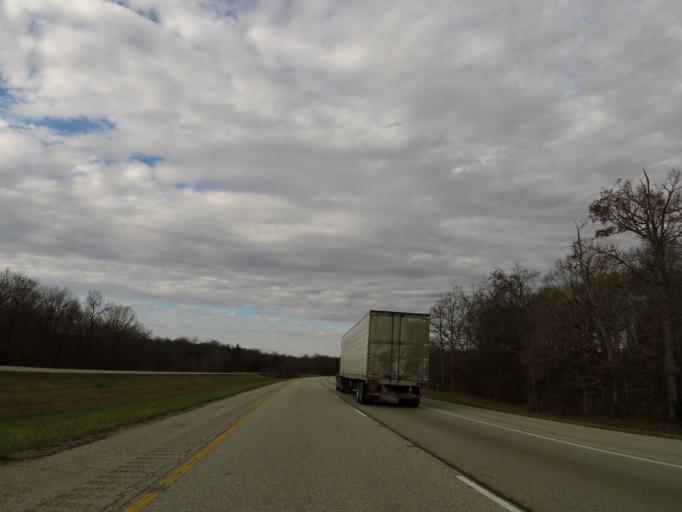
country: US
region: Illinois
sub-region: Washington County
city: Nashville
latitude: 38.3909
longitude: -89.3021
